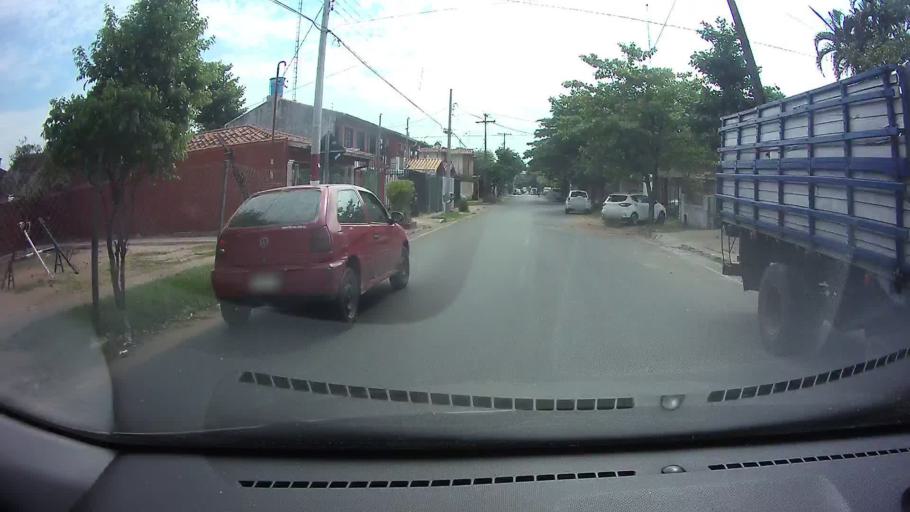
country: PY
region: Central
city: Fernando de la Mora
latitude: -25.3032
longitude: -57.5425
